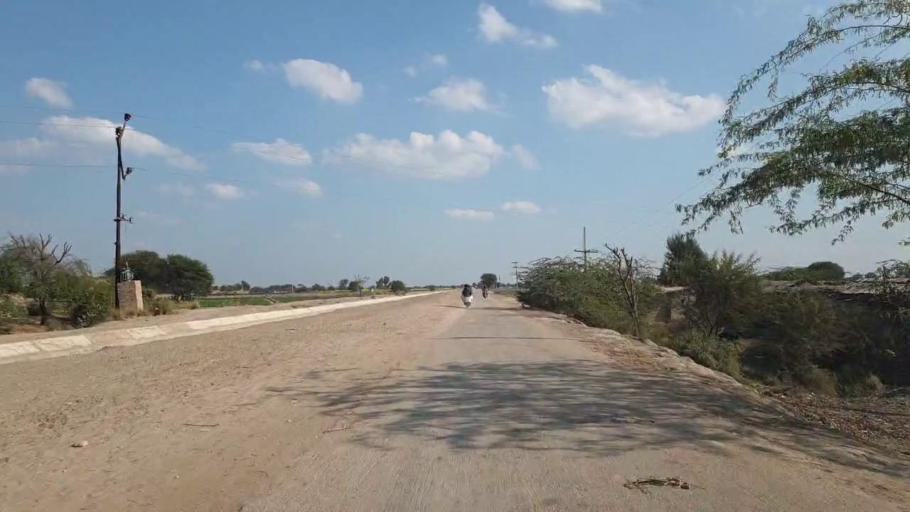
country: PK
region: Sindh
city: Shahpur Chakar
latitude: 26.1111
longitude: 68.5678
